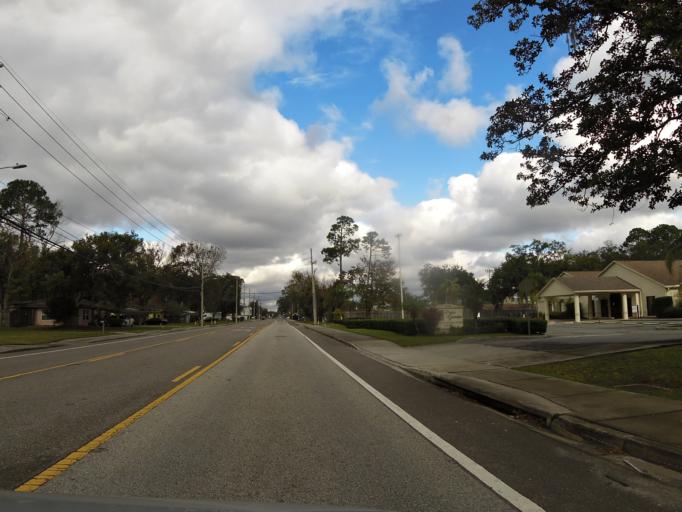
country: US
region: Florida
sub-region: Duval County
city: Jacksonville
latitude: 30.2664
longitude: -81.6083
